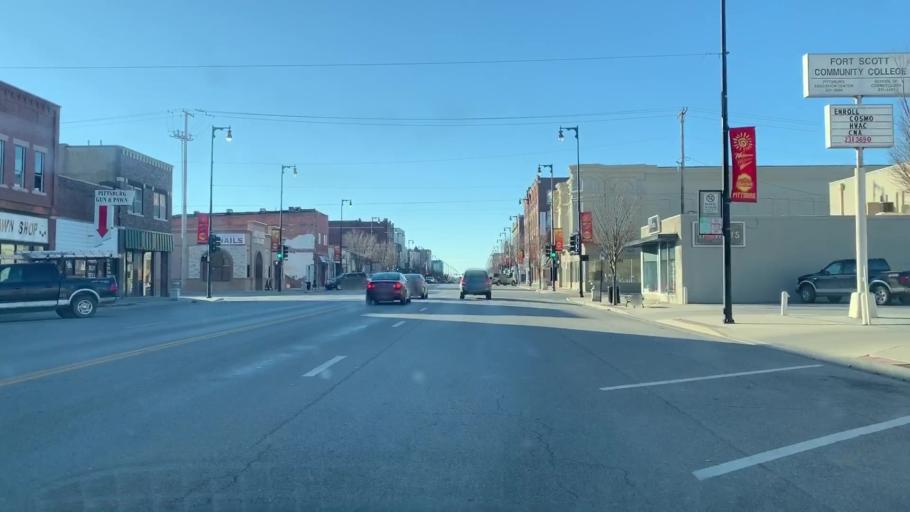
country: US
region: Kansas
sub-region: Crawford County
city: Pittsburg
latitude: 37.4156
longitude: -94.7050
